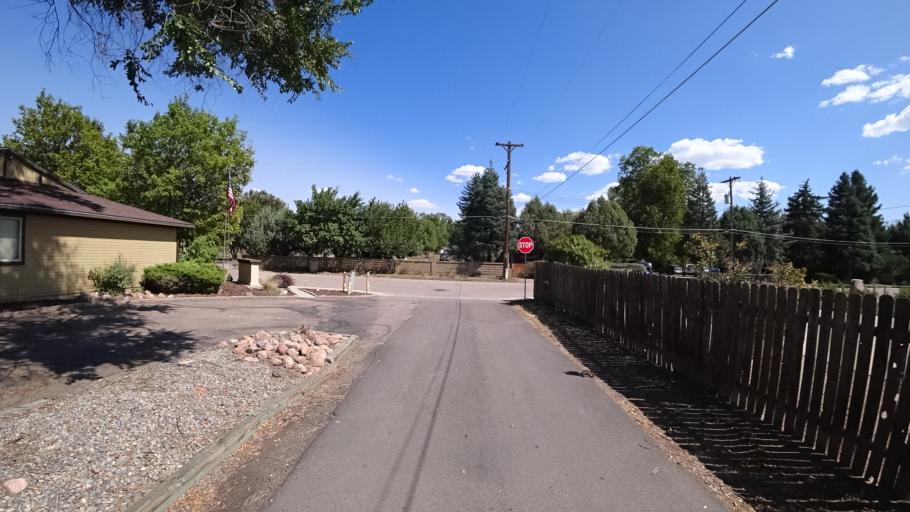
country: US
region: Colorado
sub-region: El Paso County
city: Colorado Springs
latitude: 38.8763
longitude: -104.8114
